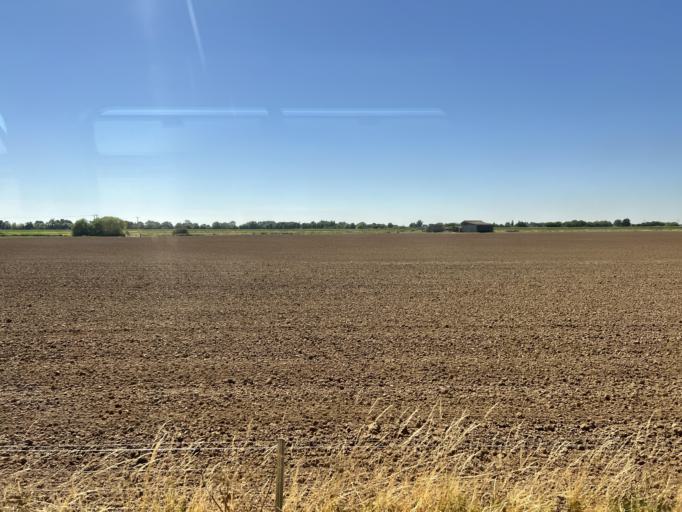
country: GB
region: England
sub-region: Lincolnshire
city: Wainfleet All Saints
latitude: 53.1168
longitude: 0.2093
